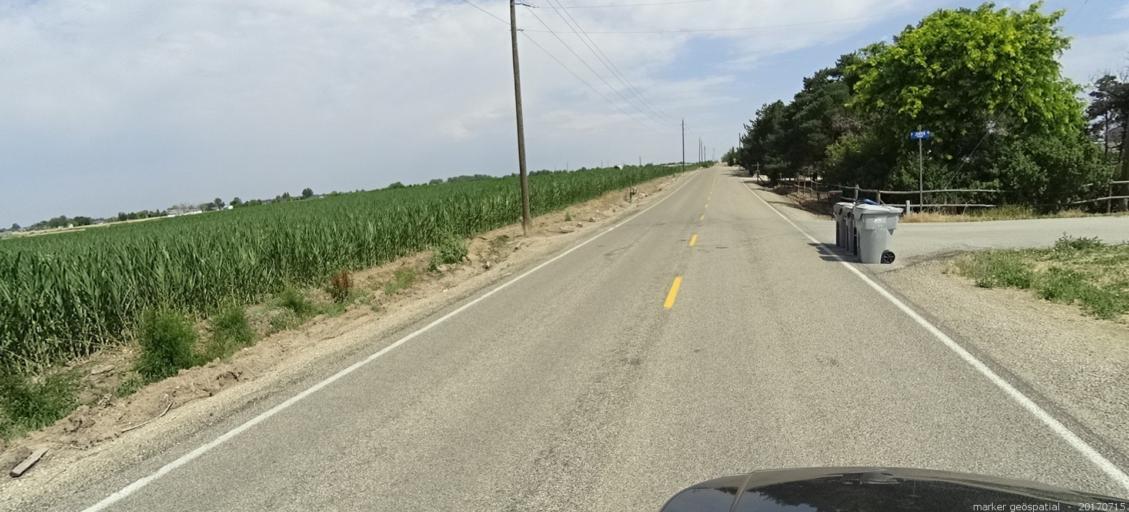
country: US
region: Idaho
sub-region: Ada County
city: Garden City
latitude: 43.5338
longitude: -116.2742
